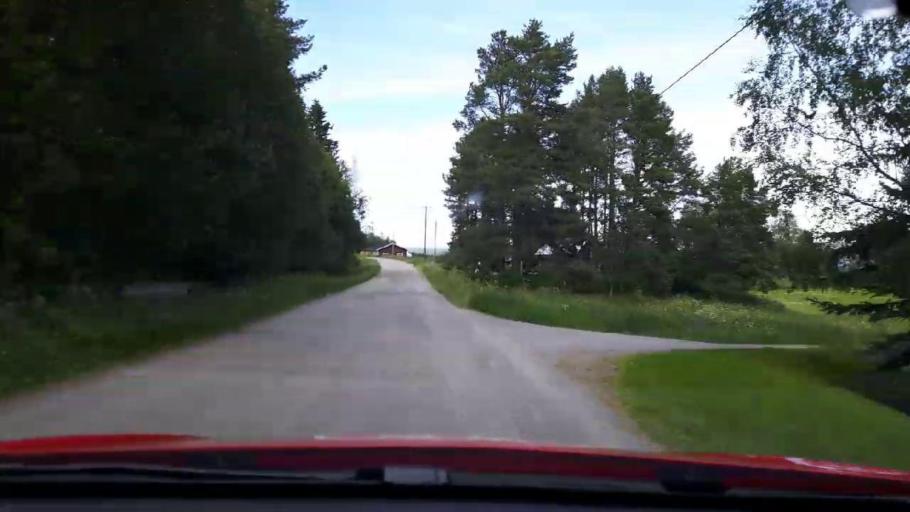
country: SE
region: Jaemtland
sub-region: Bergs Kommun
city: Hoverberg
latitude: 62.8197
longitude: 14.4598
